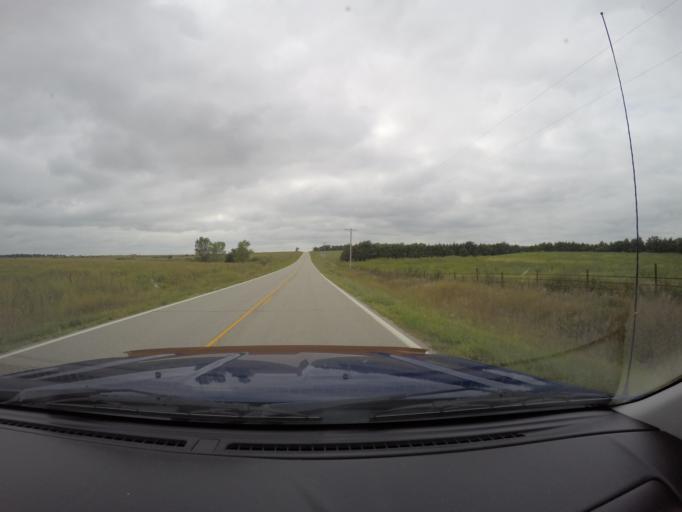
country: US
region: Kansas
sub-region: Morris County
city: Council Grove
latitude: 38.7977
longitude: -96.6436
